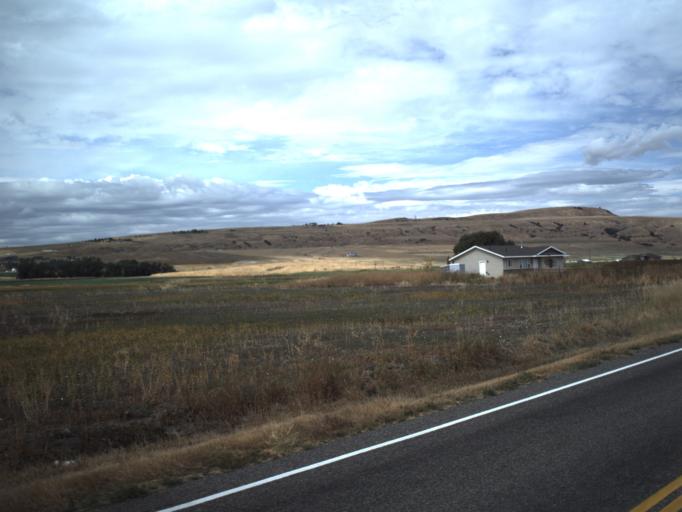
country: US
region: Utah
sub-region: Cache County
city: Mendon
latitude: 41.7635
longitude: -111.9799
